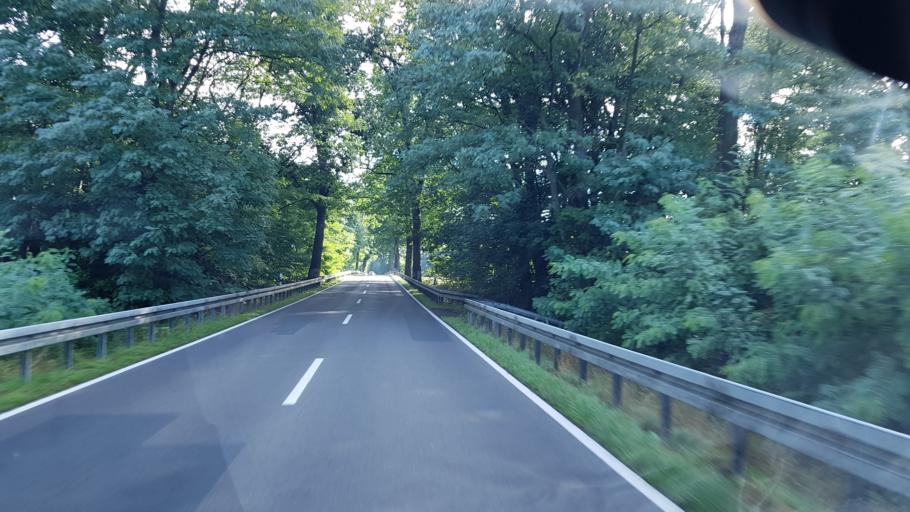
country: DE
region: Brandenburg
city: Spremberg
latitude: 51.6016
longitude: 14.4603
